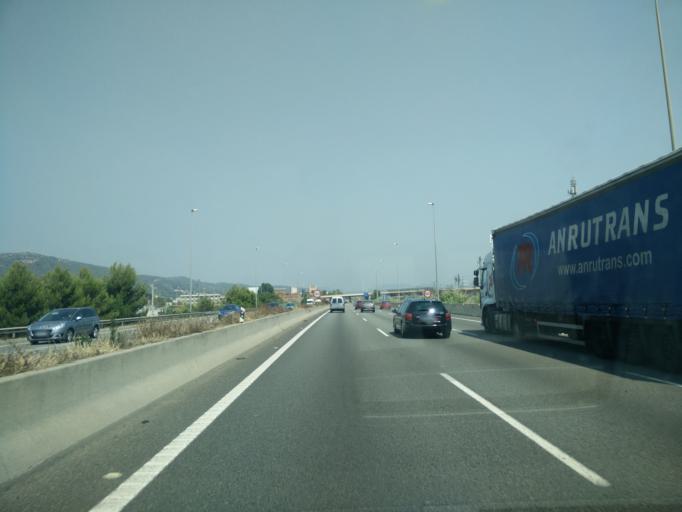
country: ES
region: Catalonia
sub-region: Provincia de Barcelona
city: Sant Vicenc dels Horts
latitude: 41.4038
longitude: 2.0122
